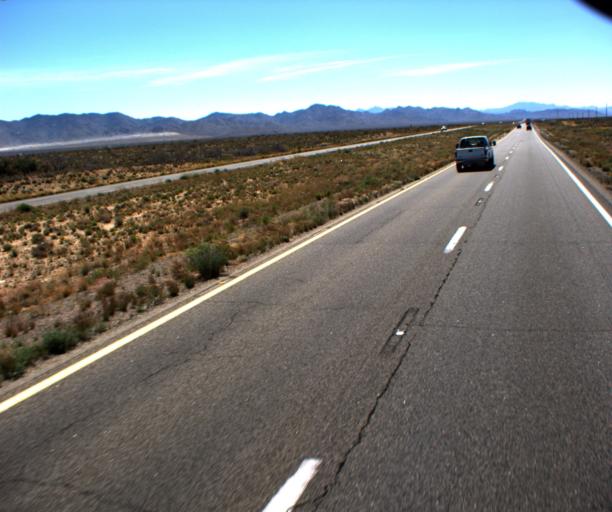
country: US
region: Arizona
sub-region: Mohave County
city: Golden Valley
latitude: 35.3622
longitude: -114.2345
